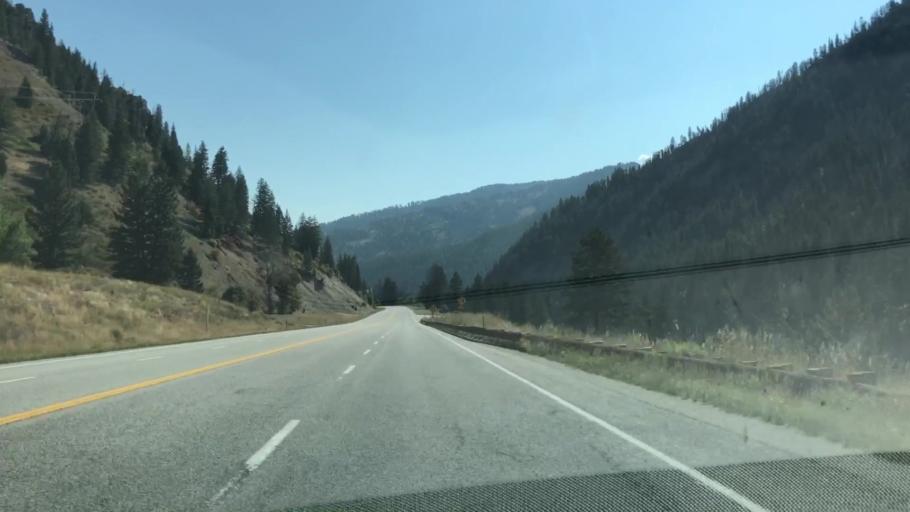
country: US
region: Wyoming
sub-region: Teton County
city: Hoback
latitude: 43.1973
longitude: -110.8936
